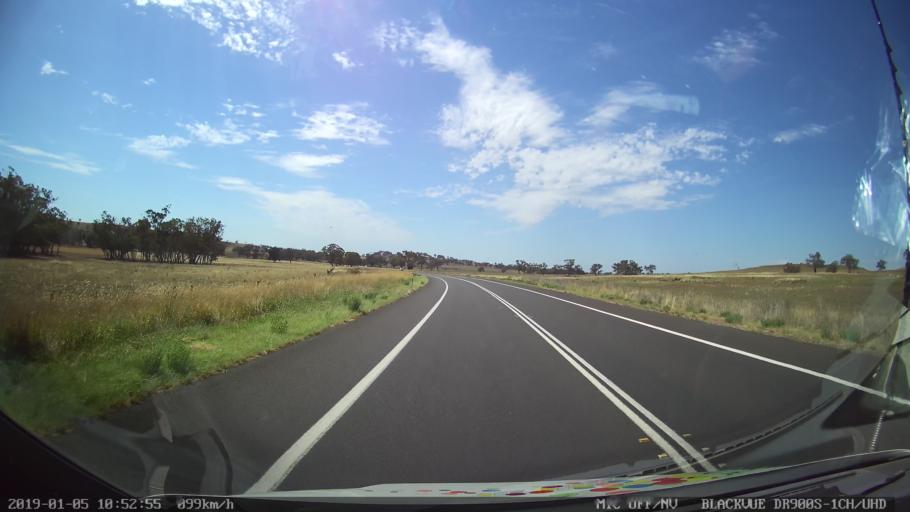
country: AU
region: New South Wales
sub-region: Warrumbungle Shire
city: Coonabarabran
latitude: -31.4381
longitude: 149.1067
